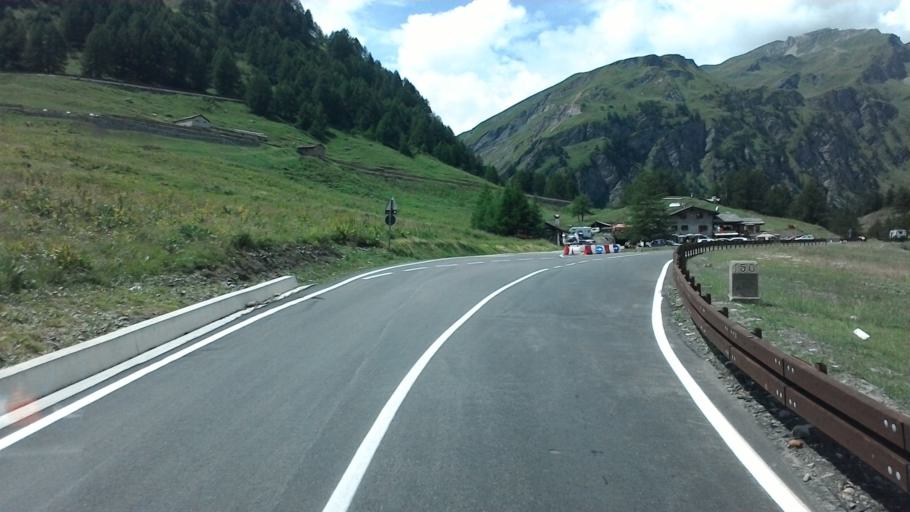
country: IT
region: Aosta Valley
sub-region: Valle d'Aosta
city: La Thuile
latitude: 45.7091
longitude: 6.9163
